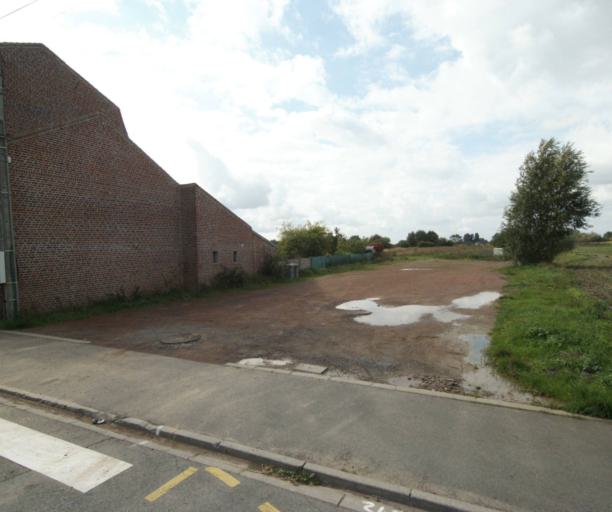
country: FR
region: Nord-Pas-de-Calais
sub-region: Departement du Nord
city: Perenchies
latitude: 50.6767
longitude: 2.9650
